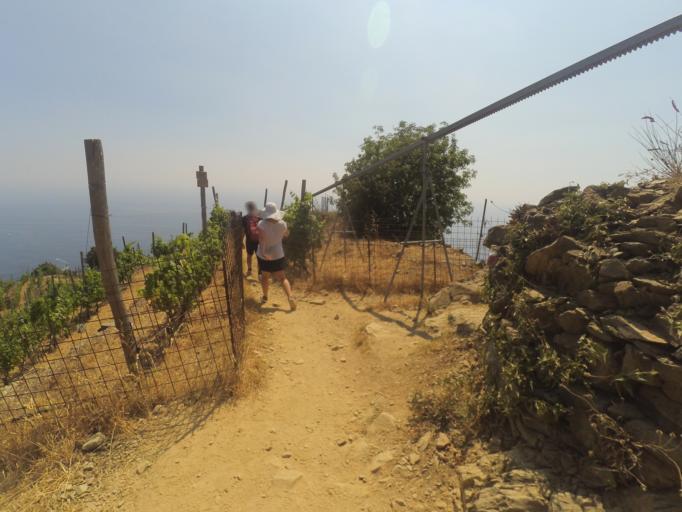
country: IT
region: Liguria
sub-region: Provincia di La Spezia
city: Riomaggiore
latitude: 44.1047
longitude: 9.7329
